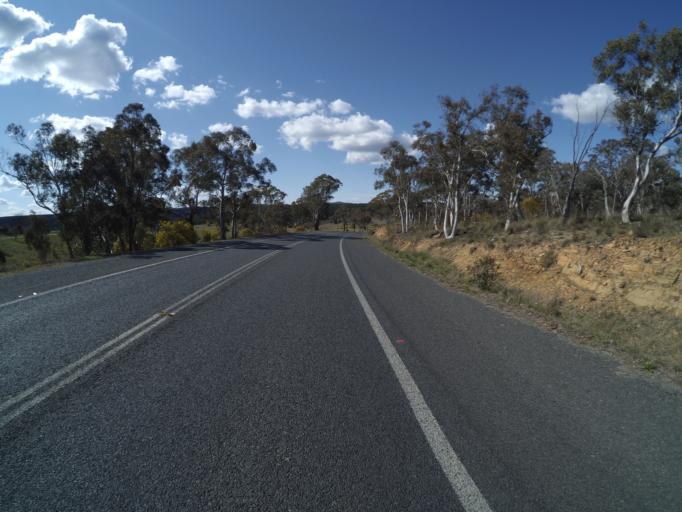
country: AU
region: New South Wales
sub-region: Queanbeyan
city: Queanbeyan
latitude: -35.3417
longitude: 149.2834
